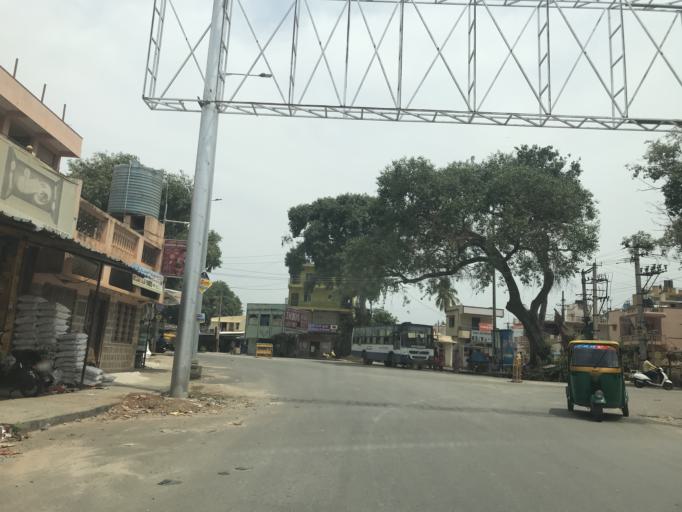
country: IN
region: Karnataka
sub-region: Bangalore Urban
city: Yelahanka
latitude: 13.0935
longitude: 77.6543
